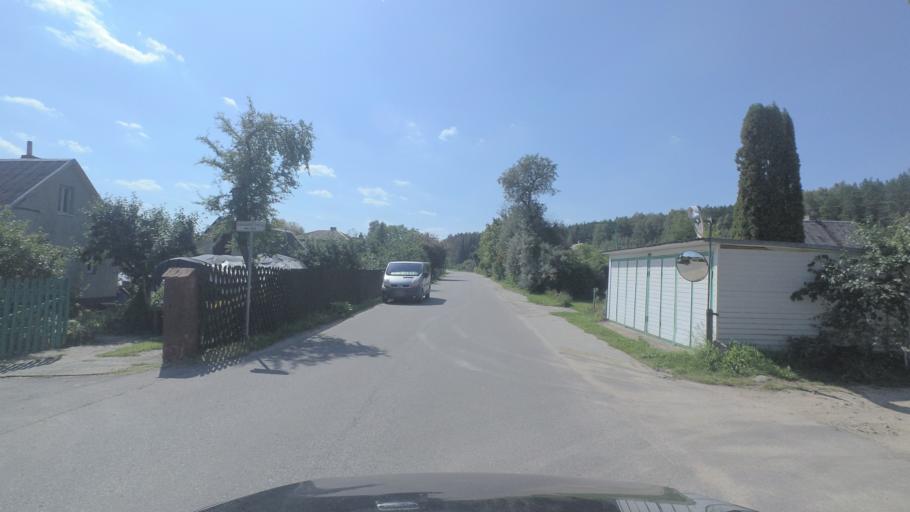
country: LT
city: Nemencine
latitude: 54.8558
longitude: 25.3810
